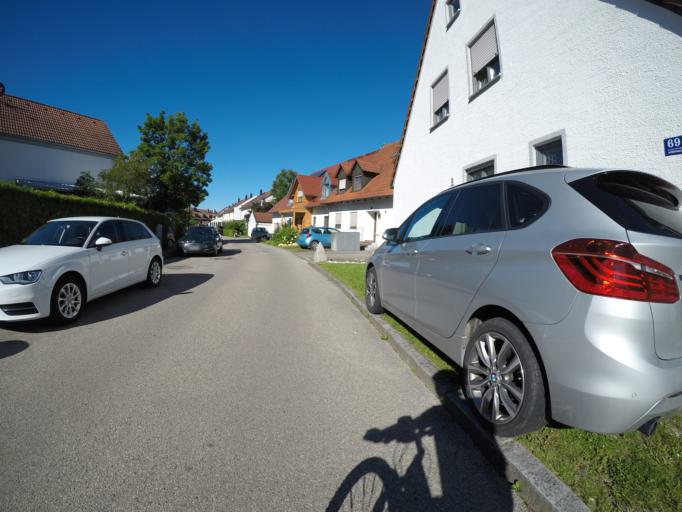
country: DE
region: Bavaria
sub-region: Upper Bavaria
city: Moosburg
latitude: 48.4584
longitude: 11.9337
